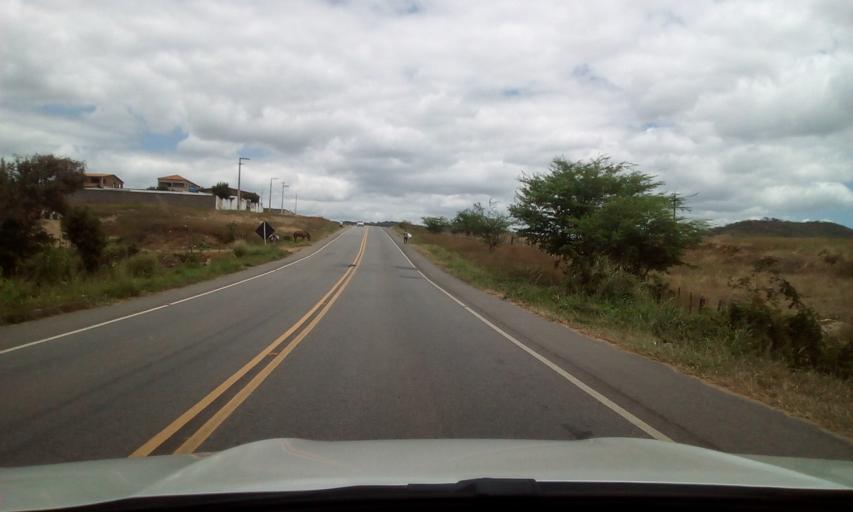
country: BR
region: Paraiba
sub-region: Serra Redonda
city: Alagoa Grande
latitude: -7.1608
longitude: -35.5962
